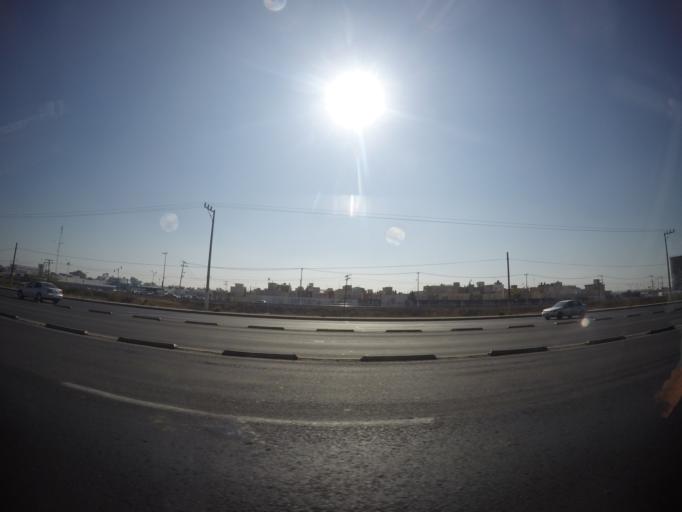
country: MX
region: Mexico
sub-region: Atenco
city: Colonia el Salado
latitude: 19.5935
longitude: -99.0209
